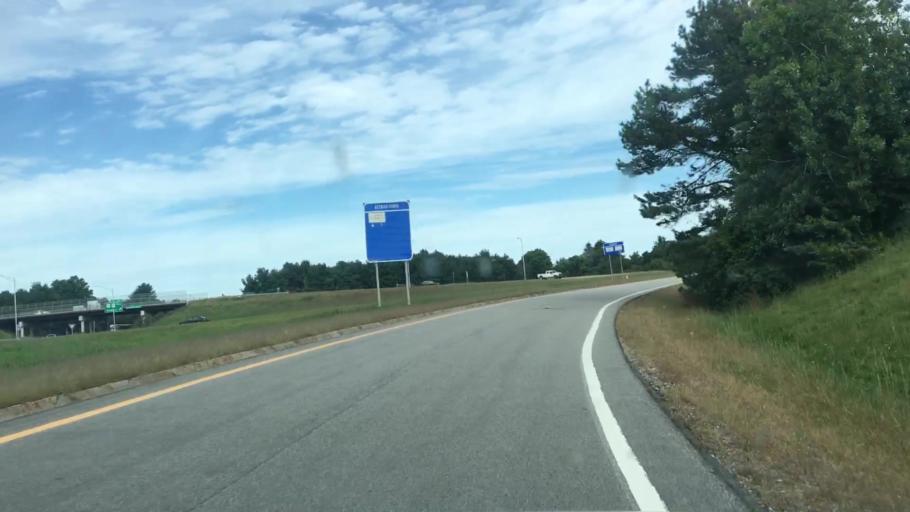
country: US
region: New Hampshire
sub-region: Strafford County
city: Dover
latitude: 43.1840
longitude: -70.8842
